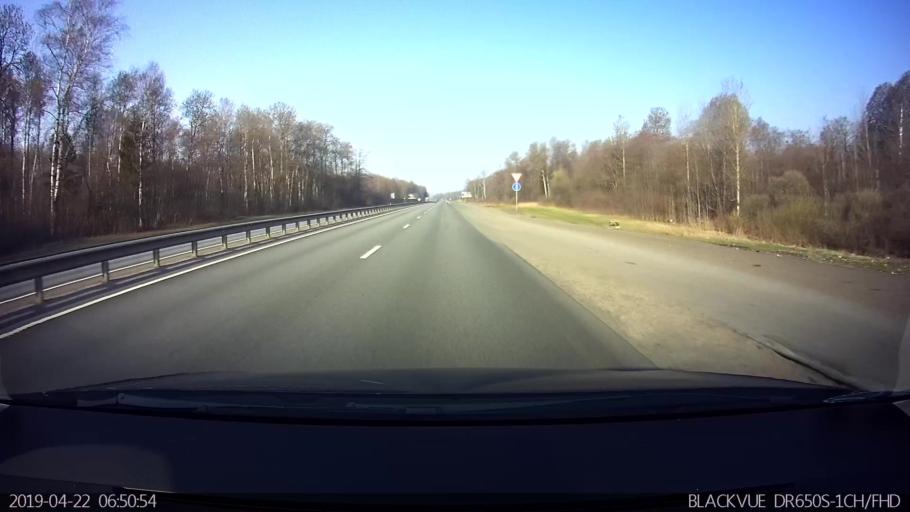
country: RU
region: Smolensk
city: Gagarin
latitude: 55.4951
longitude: 34.9937
